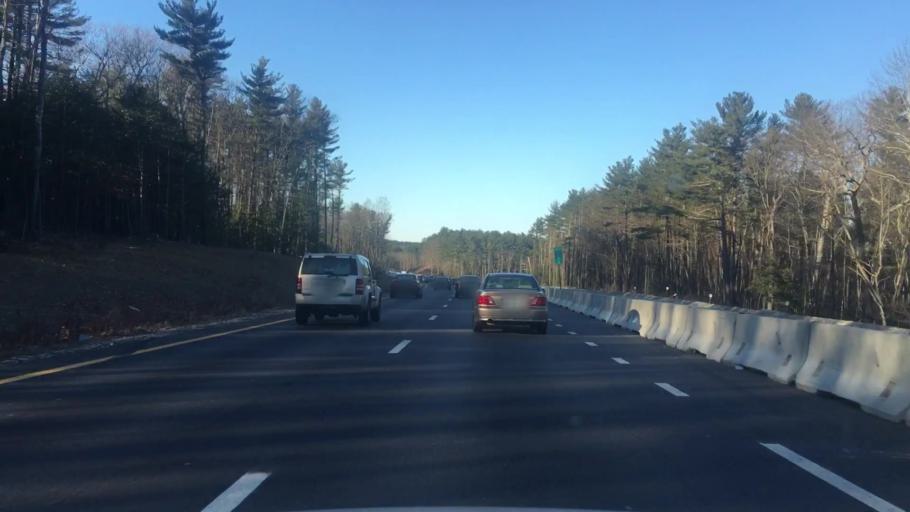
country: US
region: New Hampshire
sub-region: Rockingham County
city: Londonderry
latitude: 42.9332
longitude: -71.3812
